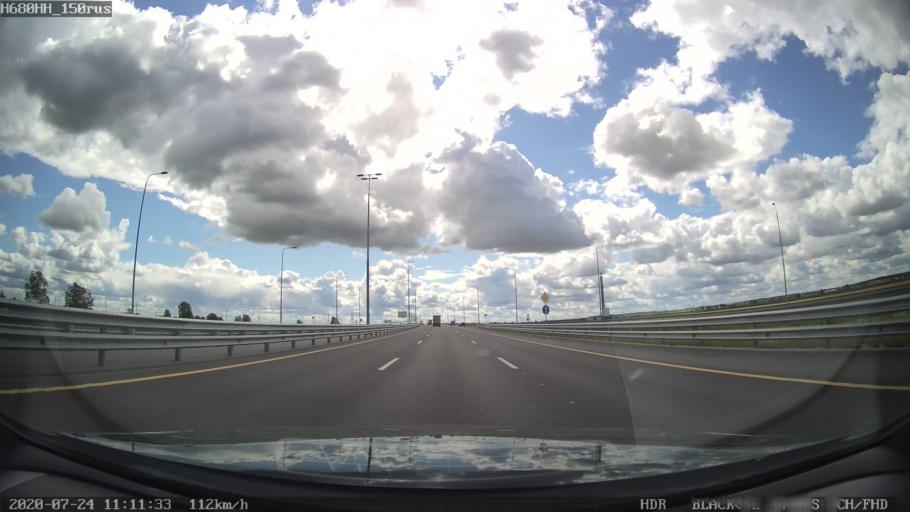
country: RU
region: Leningrad
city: Fedorovskoye
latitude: 59.7211
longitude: 30.5171
